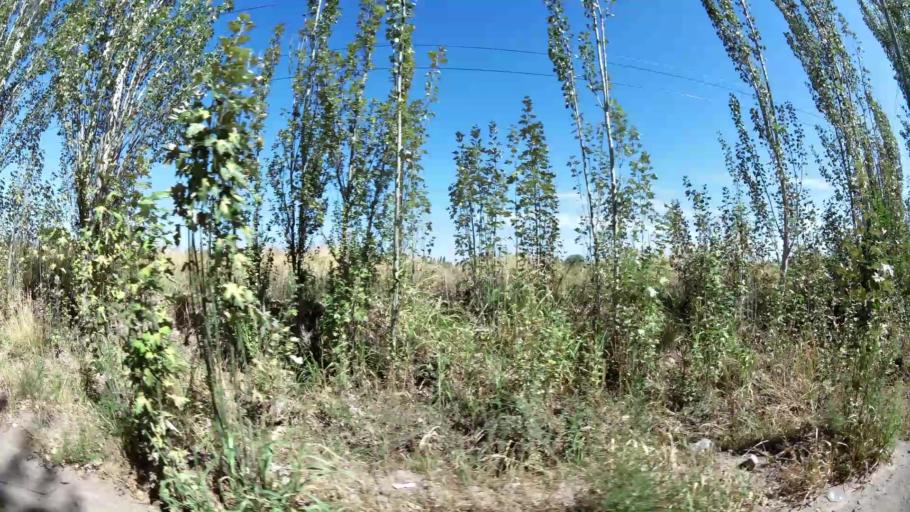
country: AR
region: Mendoza
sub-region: Departamento de Godoy Cruz
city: Godoy Cruz
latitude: -32.9852
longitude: -68.8465
